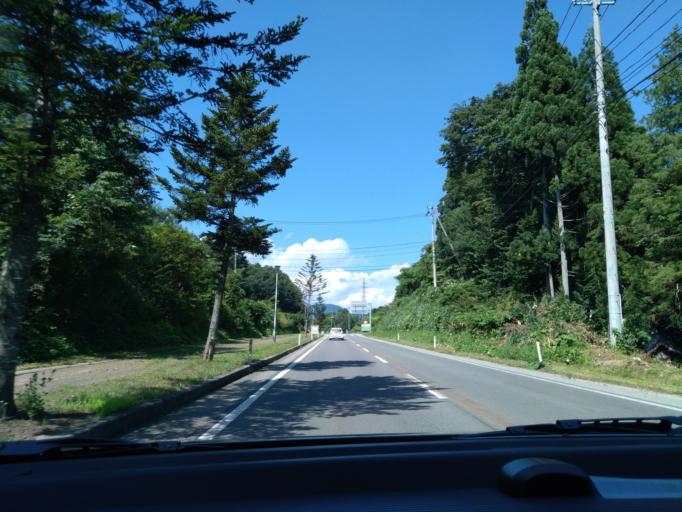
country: JP
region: Akita
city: Kakunodatemachi
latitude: 39.7405
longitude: 140.7183
